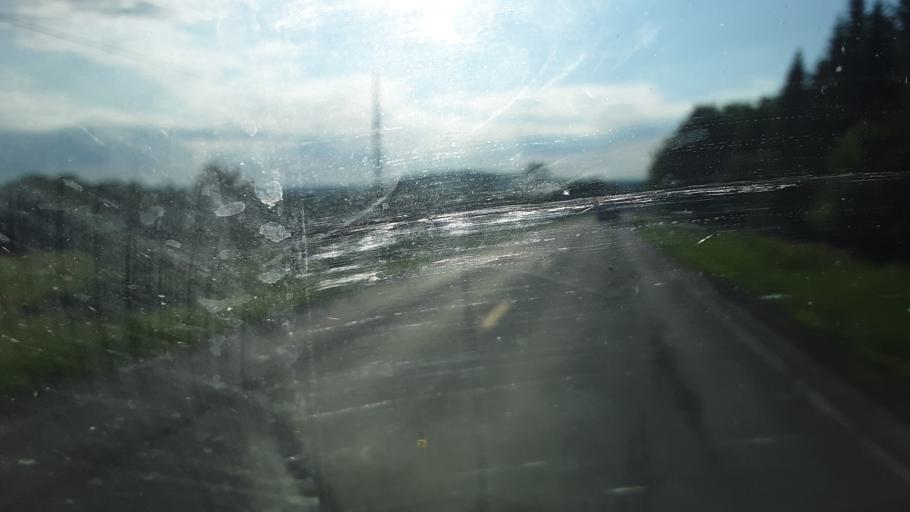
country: US
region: Maine
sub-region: Penobscot County
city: Patten
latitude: 46.2064
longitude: -68.3230
